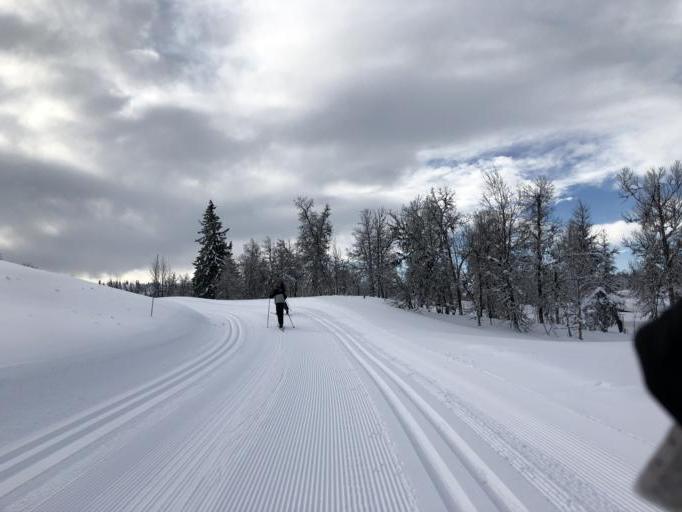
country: NO
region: Oppland
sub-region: Gausdal
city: Segalstad bru
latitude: 61.3133
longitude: 10.0675
